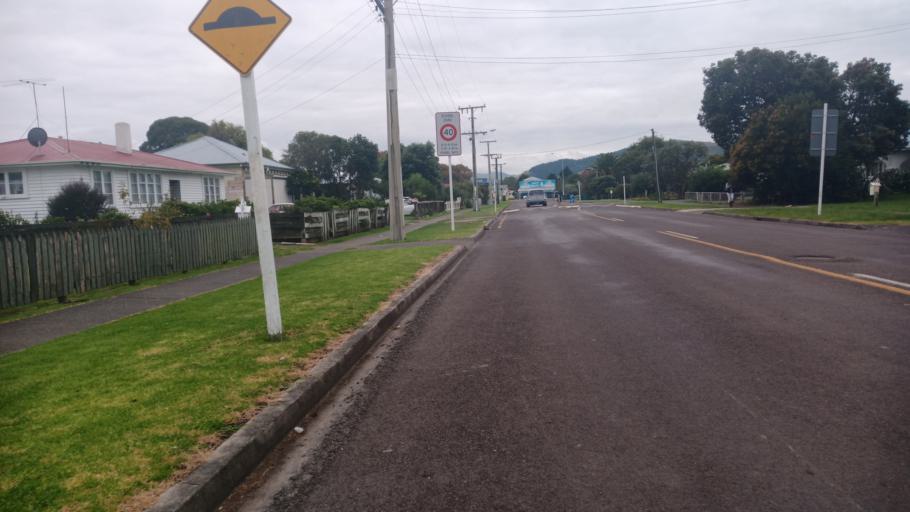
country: NZ
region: Gisborne
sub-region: Gisborne District
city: Gisborne
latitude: -38.6763
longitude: 178.0425
